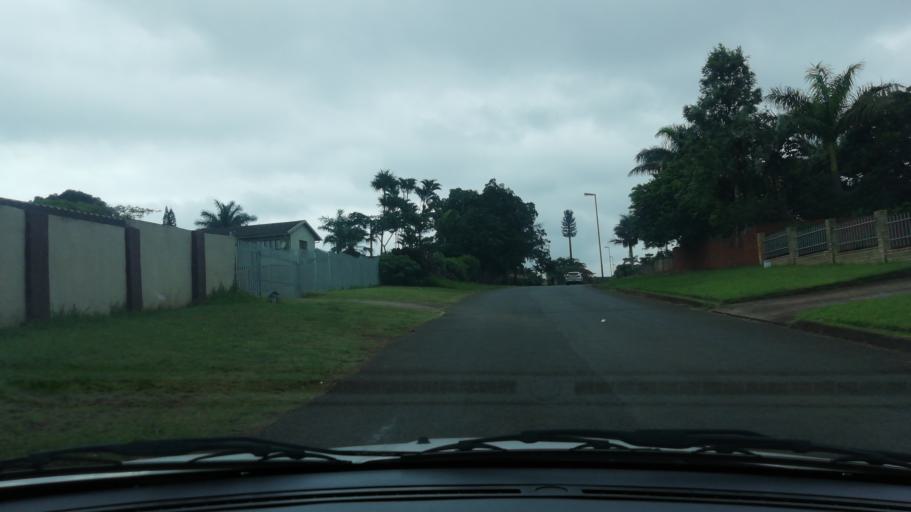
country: ZA
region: KwaZulu-Natal
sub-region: uThungulu District Municipality
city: Empangeni
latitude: -28.7650
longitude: 31.8988
